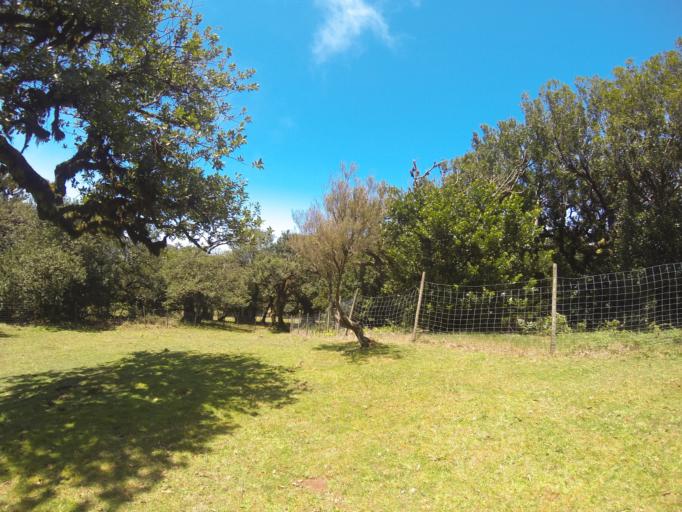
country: PT
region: Madeira
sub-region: Porto Moniz
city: Porto Moniz
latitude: 32.8106
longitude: -17.1424
